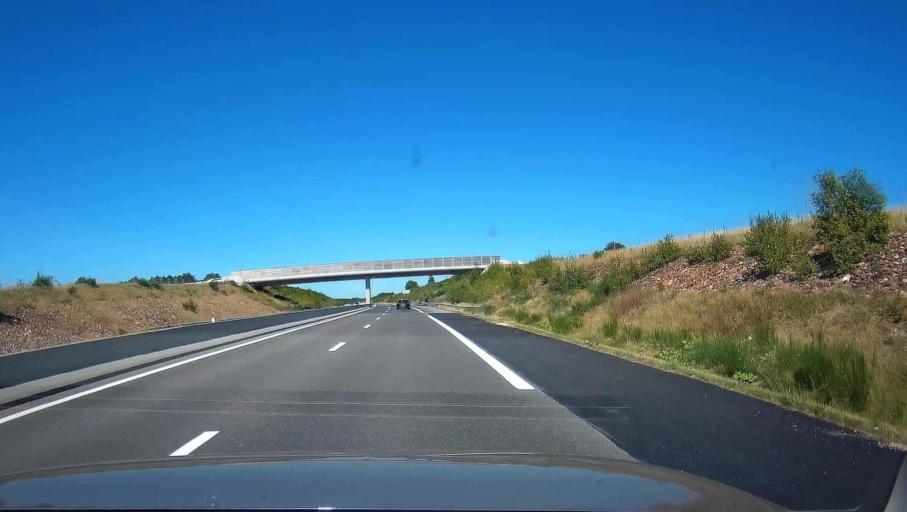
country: FR
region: Champagne-Ardenne
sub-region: Departement des Ardennes
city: Rocroi
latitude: 49.8868
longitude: 4.5185
